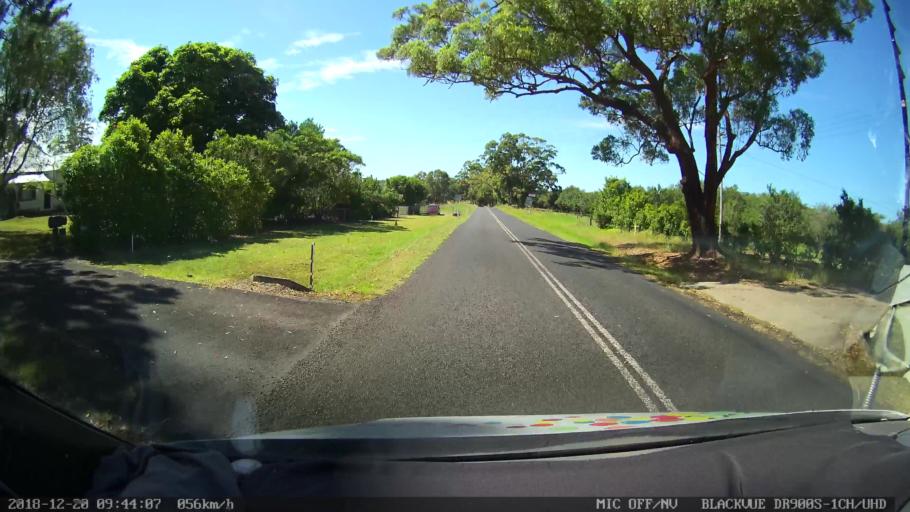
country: AU
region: New South Wales
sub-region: Lismore Municipality
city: Lismore
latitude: -28.7317
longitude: 153.2980
